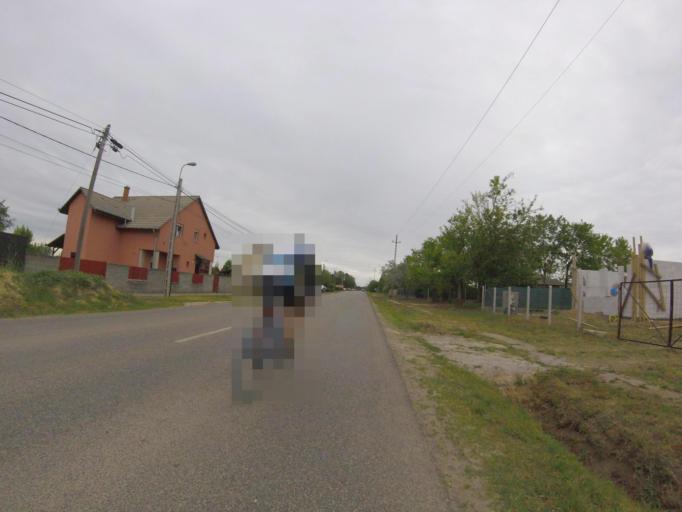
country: HU
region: Pest
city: Inarcs
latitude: 47.2513
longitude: 19.3347
